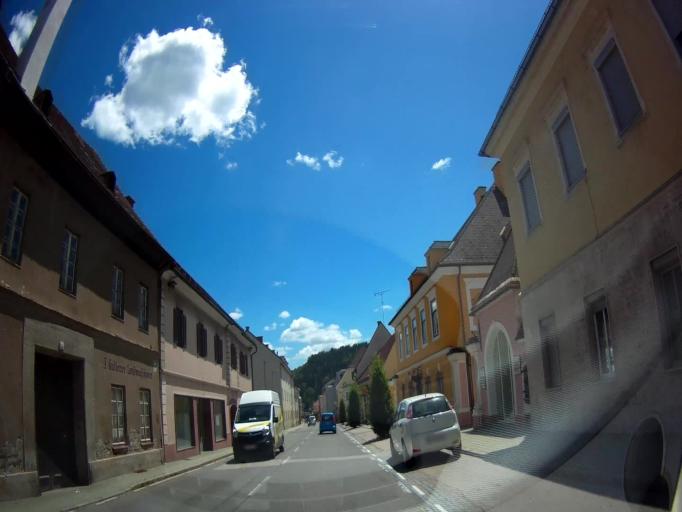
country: AT
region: Carinthia
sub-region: Politischer Bezirk Sankt Veit an der Glan
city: Sankt Veit an der Glan
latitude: 46.7656
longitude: 14.3606
